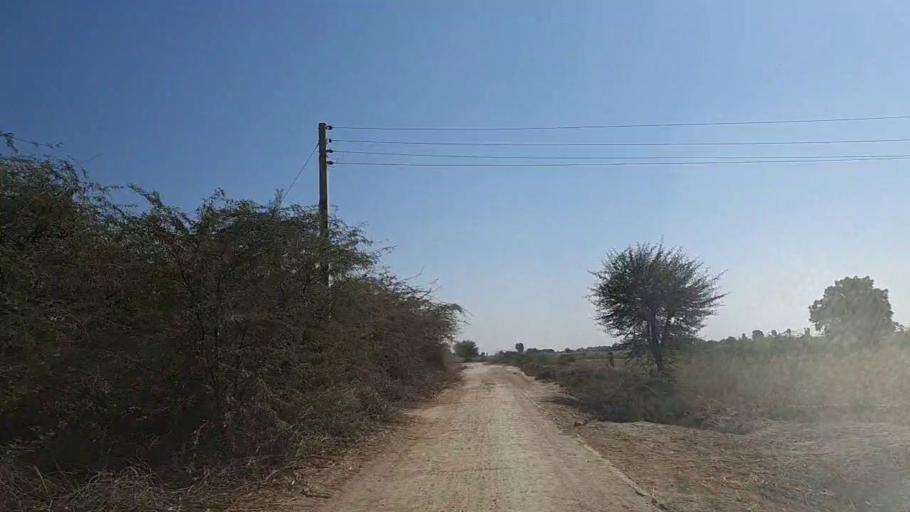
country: PK
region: Sindh
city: Naukot
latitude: 25.0364
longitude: 69.3916
